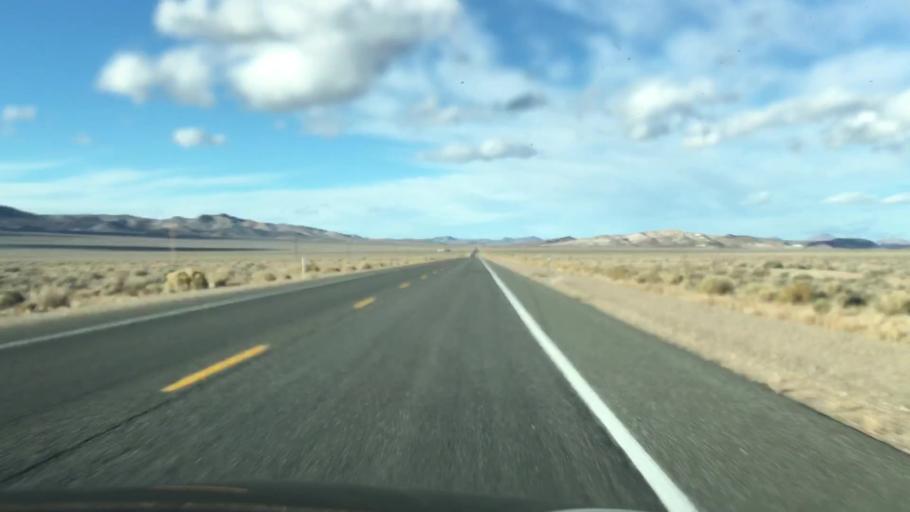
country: US
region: Nevada
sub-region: Esmeralda County
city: Goldfield
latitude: 37.4779
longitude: -117.1781
